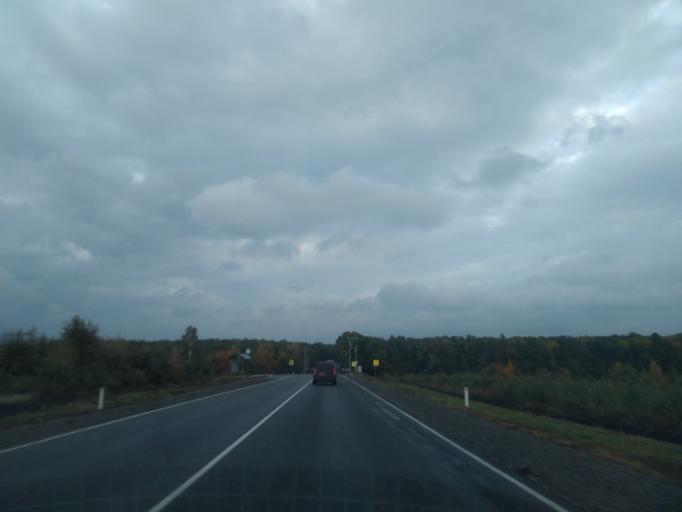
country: RU
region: Lipetsk
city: Borinskoye
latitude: 52.5907
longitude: 39.2587
